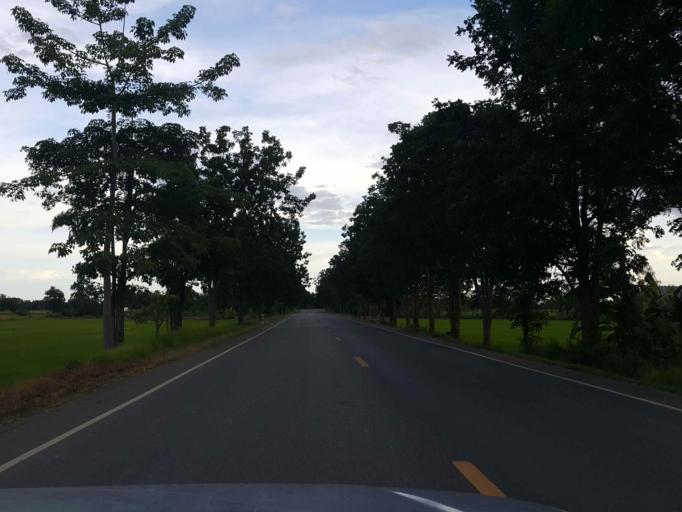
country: TH
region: Sukhothai
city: Sawankhalok
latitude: 17.3454
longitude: 99.7427
